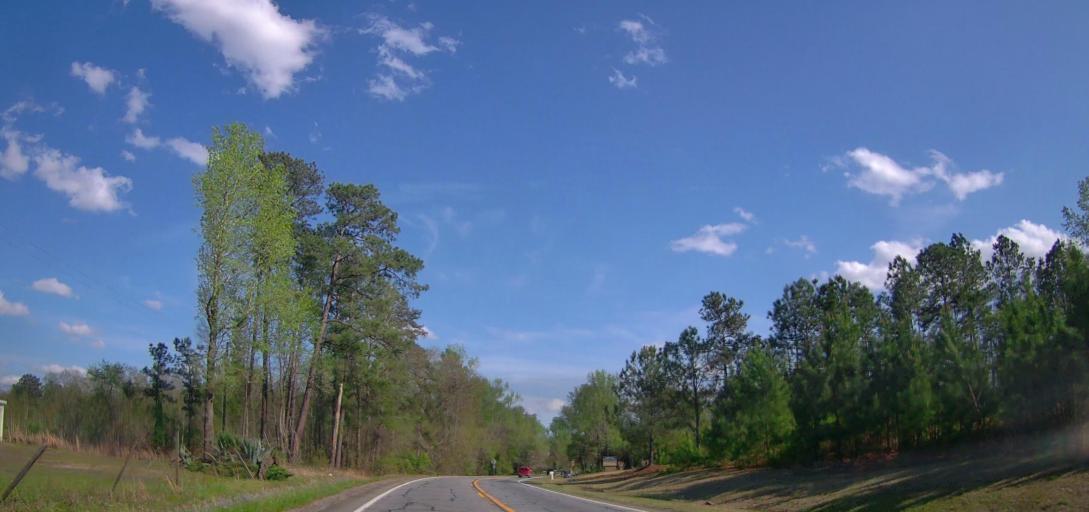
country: US
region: Georgia
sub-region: Baldwin County
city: Hardwick
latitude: 33.0890
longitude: -83.1745
